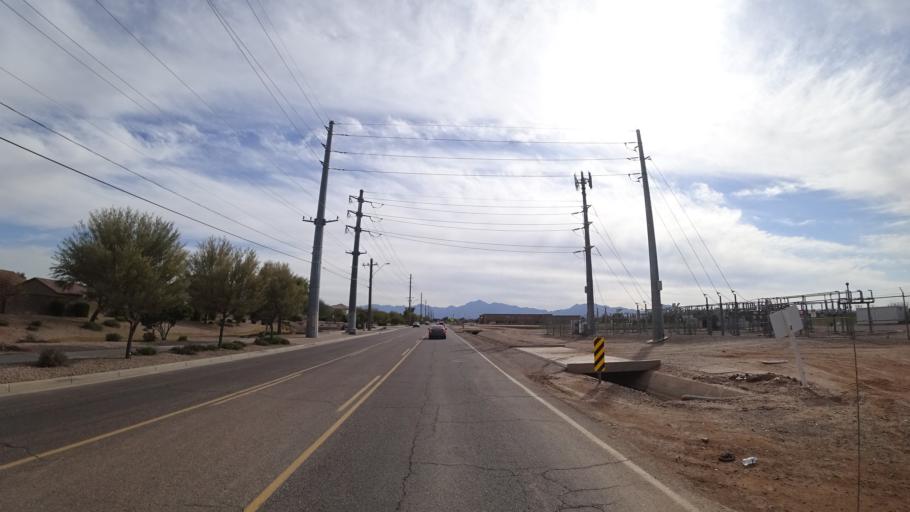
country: US
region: Arizona
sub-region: Maricopa County
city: Tolleson
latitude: 33.4267
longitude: -112.2554
